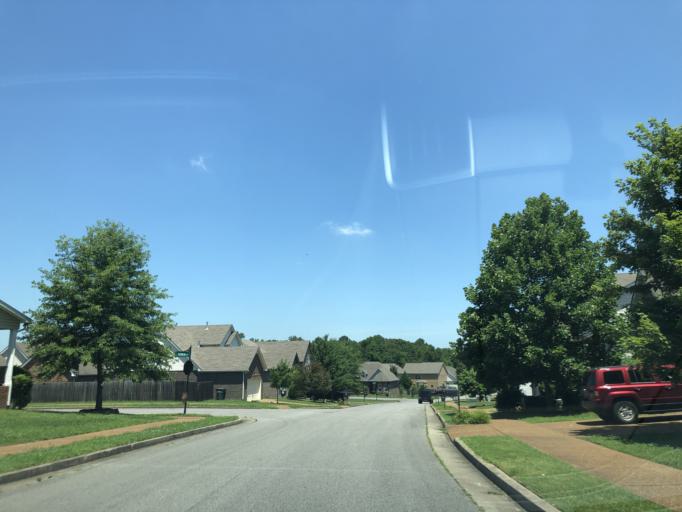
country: US
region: Tennessee
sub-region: Williamson County
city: Nolensville
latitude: 36.0180
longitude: -86.6692
